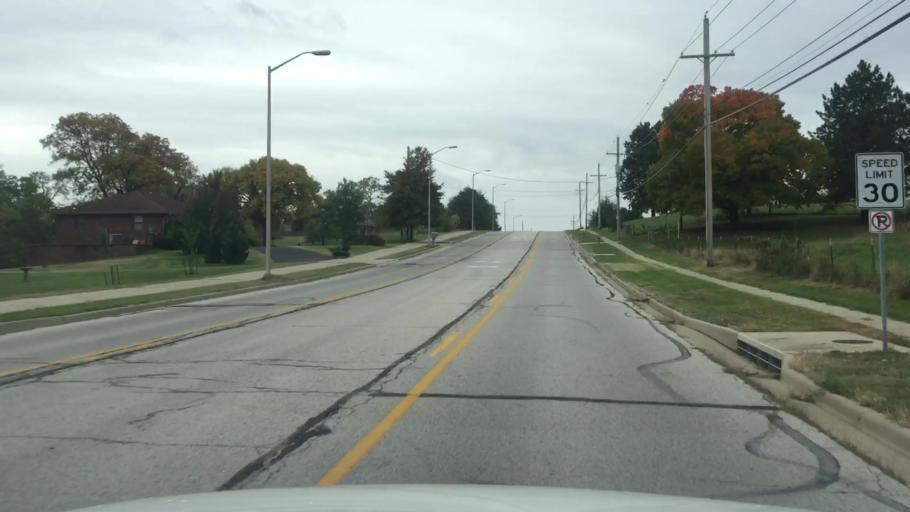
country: US
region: Kansas
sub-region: Johnson County
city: Shawnee
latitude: 39.0204
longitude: -94.7706
